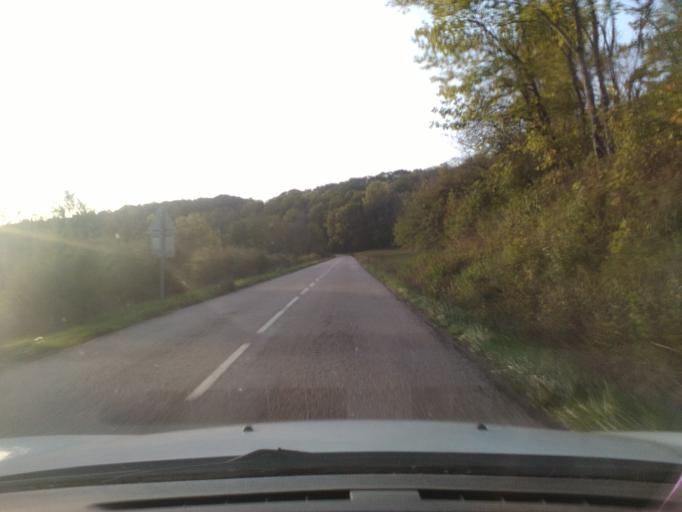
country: FR
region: Lorraine
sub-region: Departement des Vosges
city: Chatel-sur-Moselle
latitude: 48.2973
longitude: 6.4357
